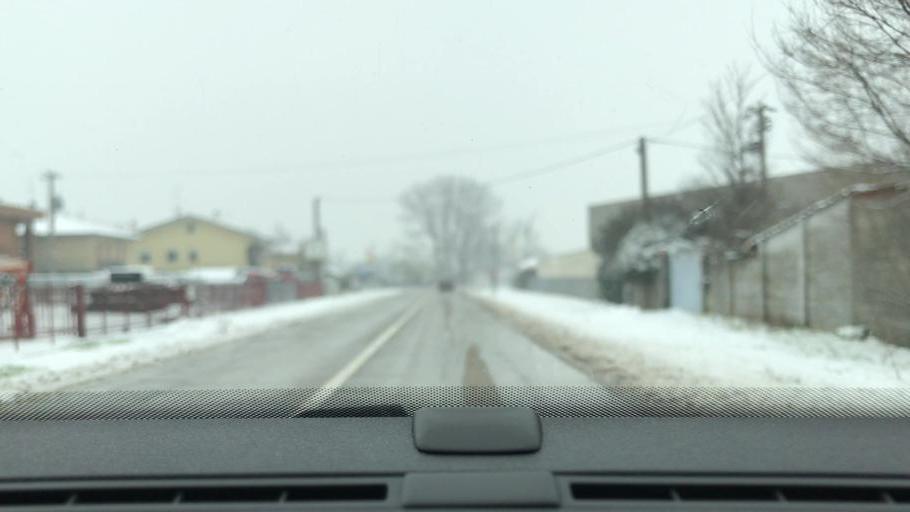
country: IT
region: Lombardy
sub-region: Provincia di Mantova
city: Goito
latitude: 45.2622
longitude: 10.6632
